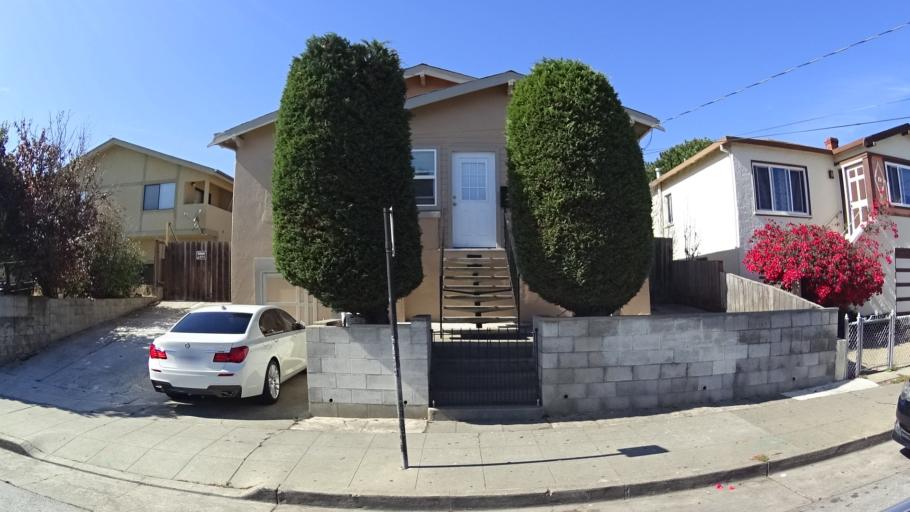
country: US
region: California
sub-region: San Mateo County
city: South San Francisco
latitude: 37.6584
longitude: -122.4090
